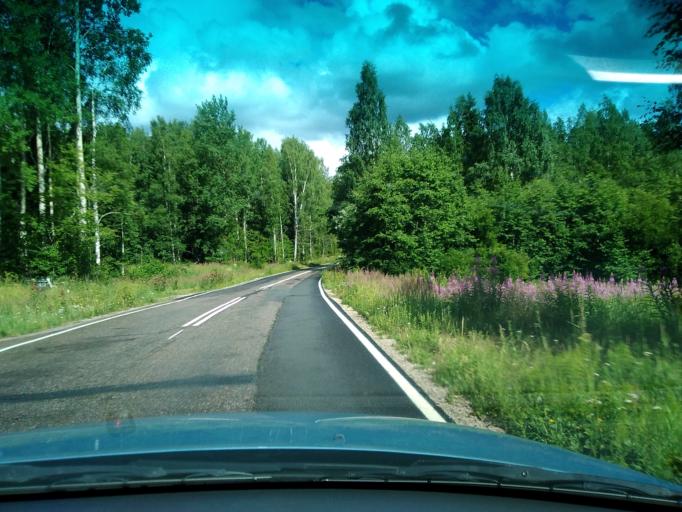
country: FI
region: Central Finland
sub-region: Saarijaervi-Viitasaari
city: Saarijaervi
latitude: 62.7349
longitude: 25.1263
